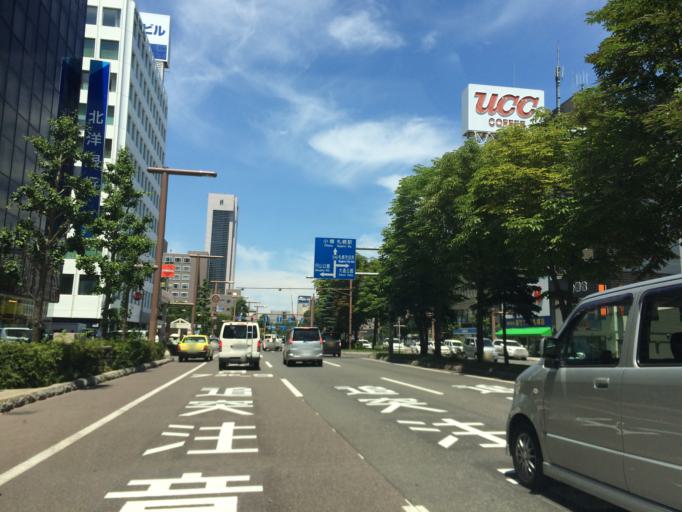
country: JP
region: Hokkaido
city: Sapporo
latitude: 43.0575
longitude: 141.3413
